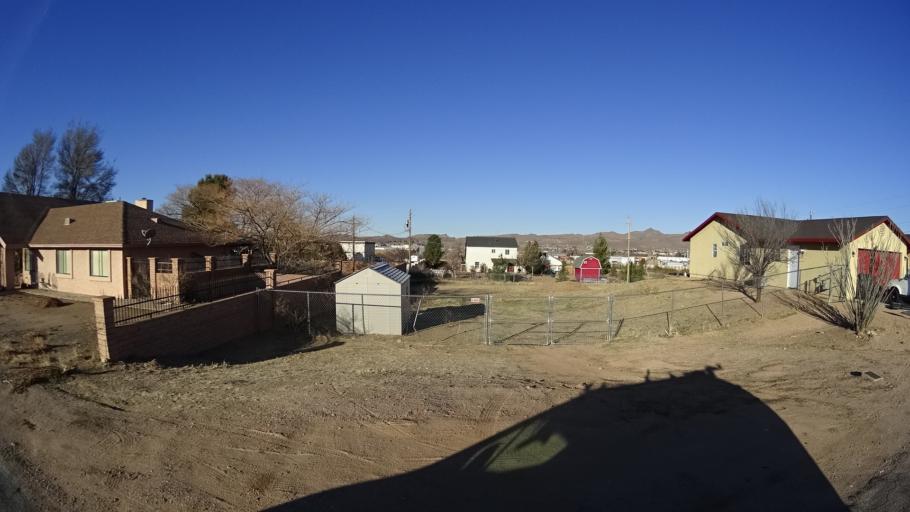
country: US
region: Arizona
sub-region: Mohave County
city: Kingman
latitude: 35.2086
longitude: -114.0100
